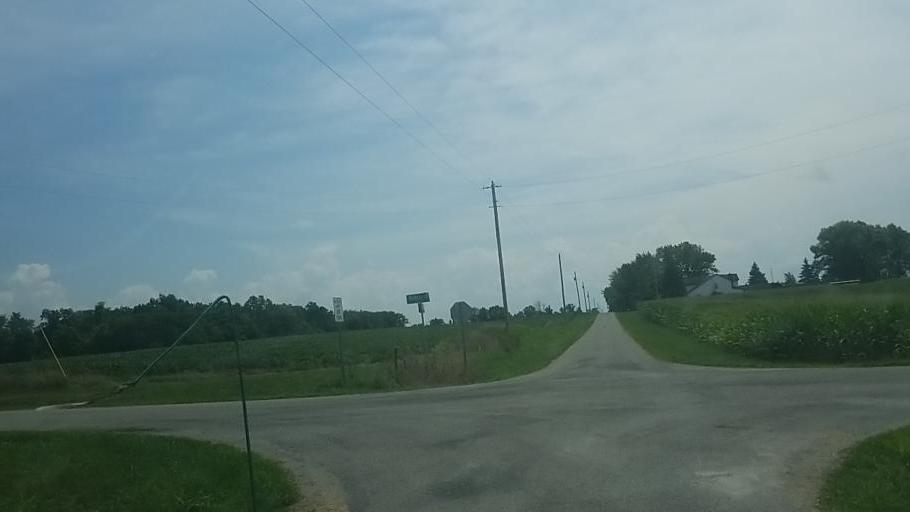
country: US
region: Ohio
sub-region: Hardin County
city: Forest
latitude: 40.6728
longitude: -83.3907
